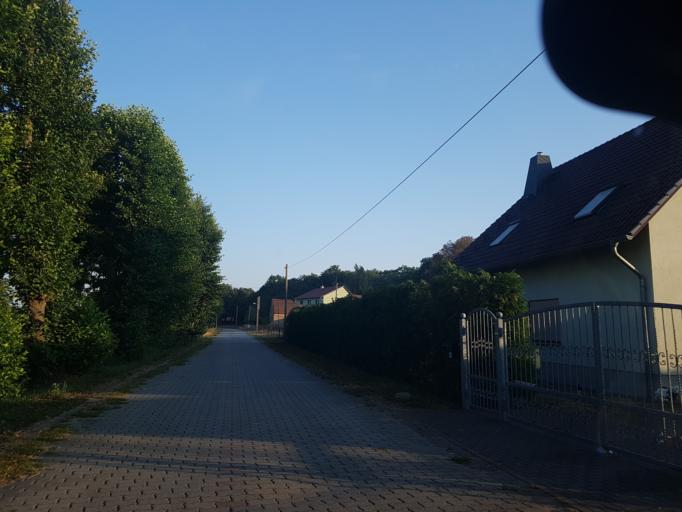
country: DE
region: Brandenburg
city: Falkenberg
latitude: 51.6429
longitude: 13.2944
